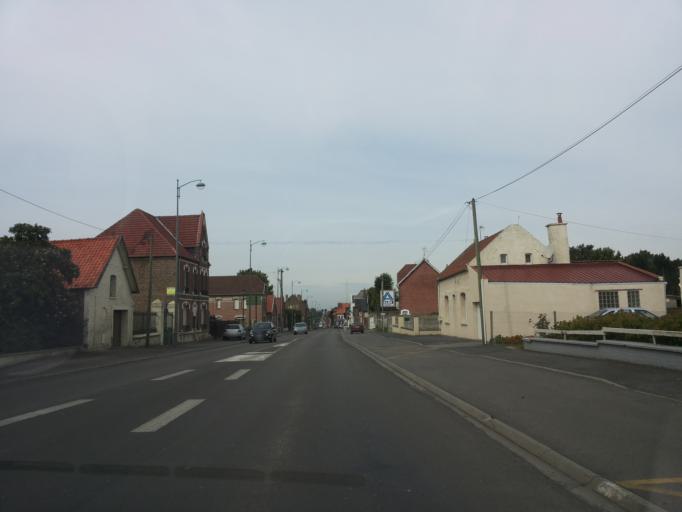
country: FR
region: Nord-Pas-de-Calais
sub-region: Departement du Pas-de-Calais
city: Marquion
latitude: 50.2097
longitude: 3.0921
